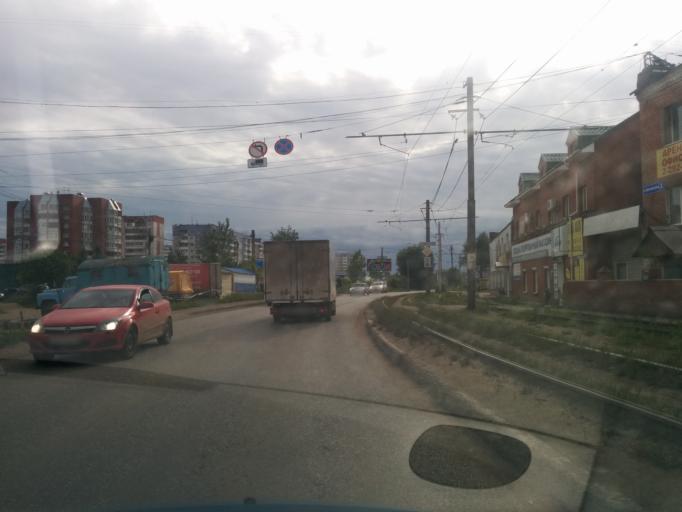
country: RU
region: Perm
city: Kondratovo
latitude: 58.0009
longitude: 56.1478
